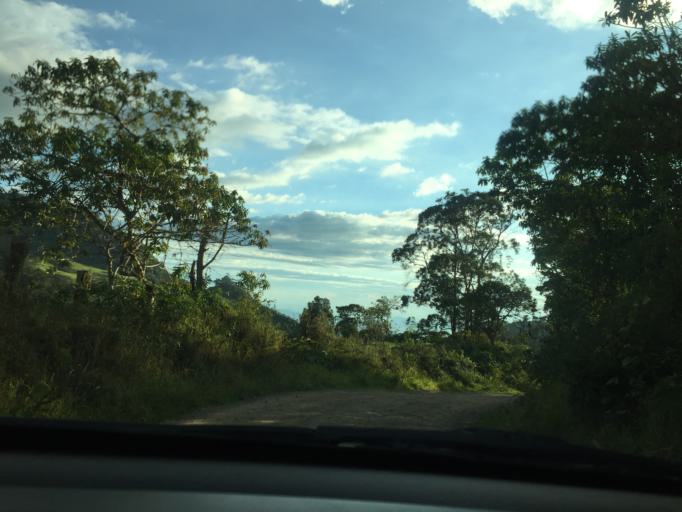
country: CO
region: Cundinamarca
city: Zipacon
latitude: 4.7253
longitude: -74.3885
